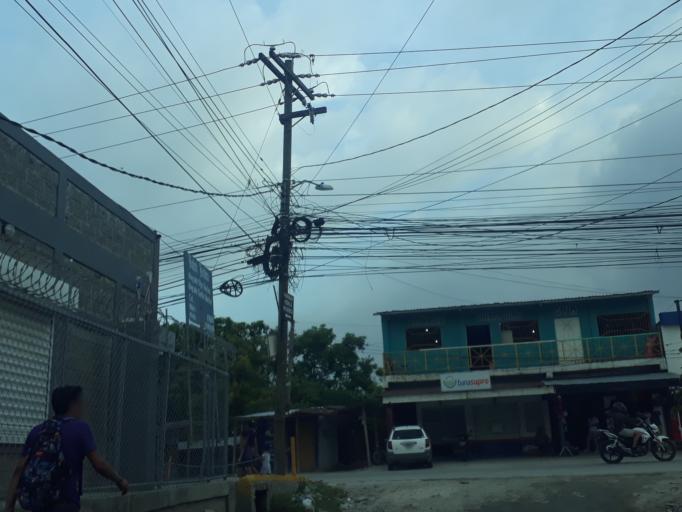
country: HN
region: Cortes
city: Choloma
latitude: 15.5726
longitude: -87.9499
